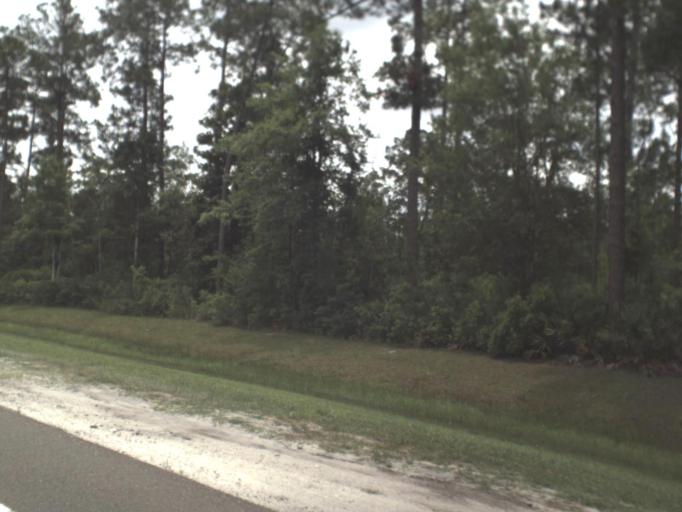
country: US
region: Florida
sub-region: Nassau County
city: Nassau Village-Ratliff
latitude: 30.4865
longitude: -81.6720
